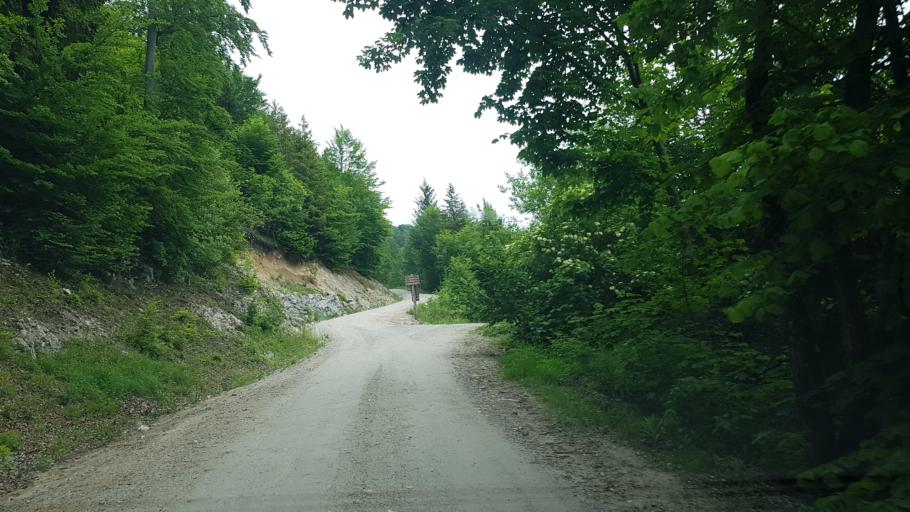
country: SI
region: Dobrna
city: Dobrna
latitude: 46.3857
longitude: 15.1959
